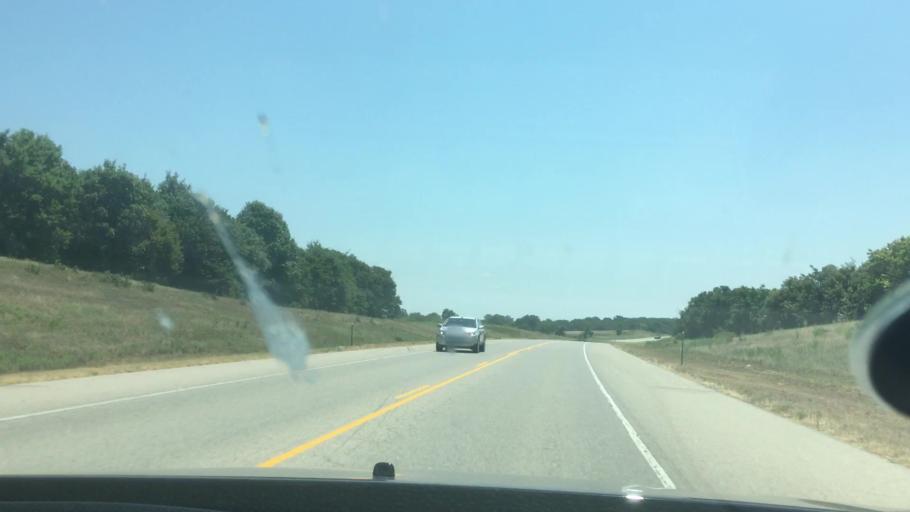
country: US
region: Oklahoma
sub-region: Pontotoc County
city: Ada
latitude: 34.6762
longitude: -96.5754
